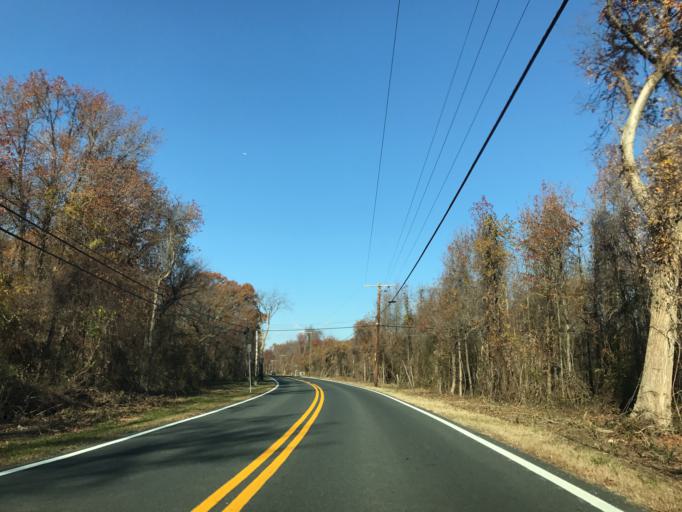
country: US
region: Maryland
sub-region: Anne Arundel County
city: Lake Shore
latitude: 39.1000
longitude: -76.4339
